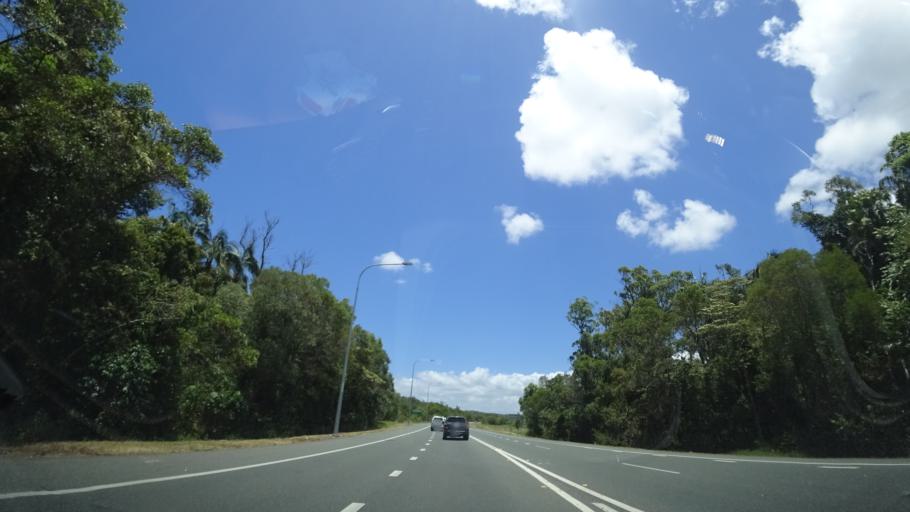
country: AU
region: Queensland
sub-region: Sunshine Coast
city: Little Mountain
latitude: -26.7585
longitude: 153.1089
